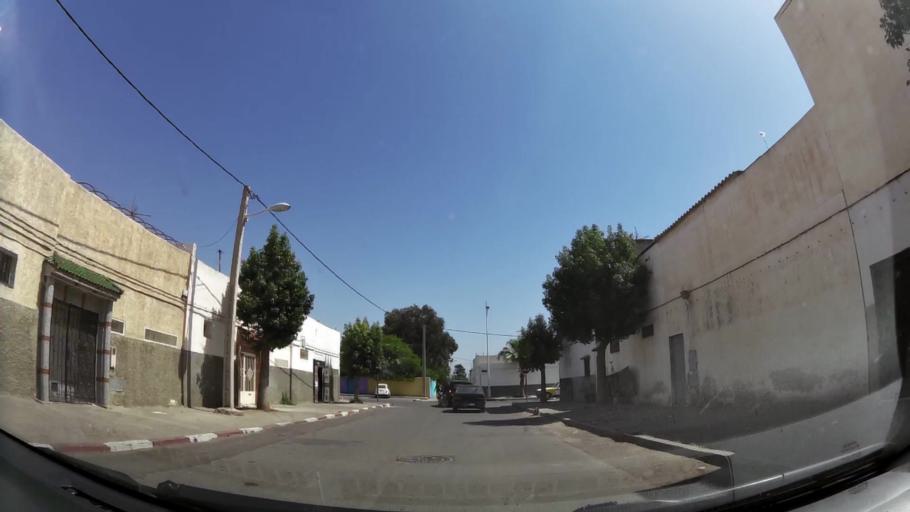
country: MA
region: Souss-Massa-Draa
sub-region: Agadir-Ida-ou-Tnan
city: Agadir
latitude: 30.4109
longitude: -9.5860
